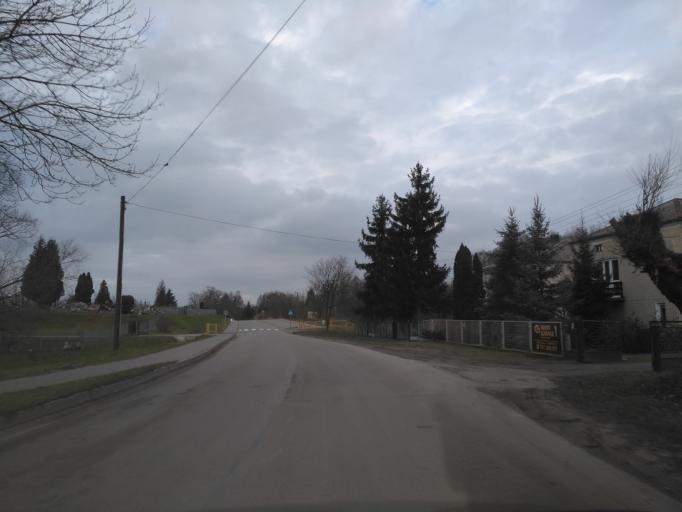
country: PL
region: Lublin Voivodeship
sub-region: Powiat leczynski
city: Cycow
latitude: 51.1993
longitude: 23.1553
